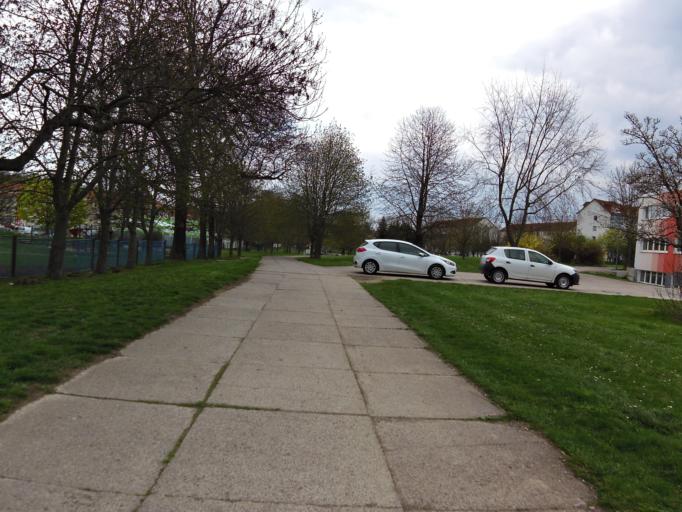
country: DE
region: Thuringia
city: Gotha
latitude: 50.9494
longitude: 10.6843
